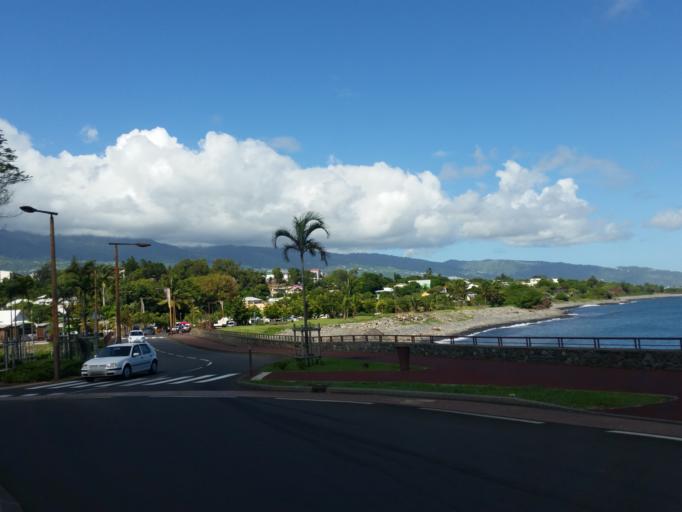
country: RE
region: Reunion
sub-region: Reunion
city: Sainte-Marie
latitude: -20.8953
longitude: 55.5518
